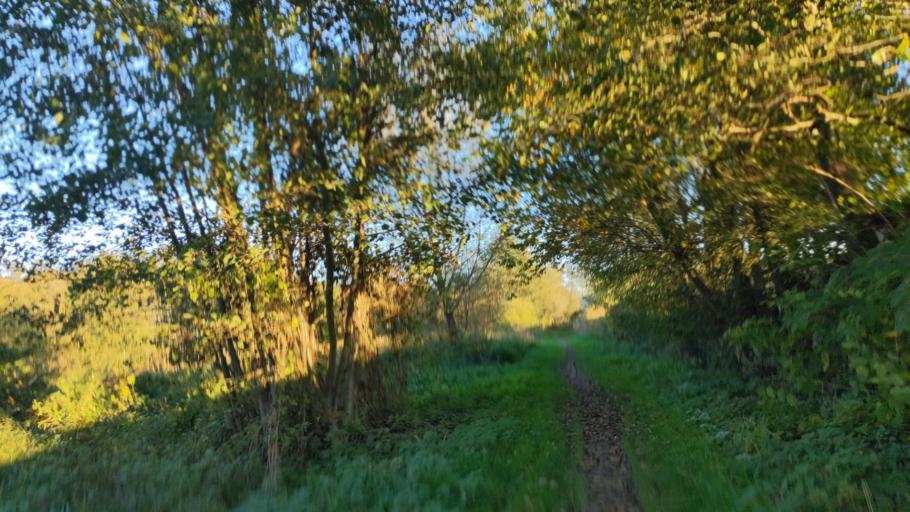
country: DE
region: Schleswig-Holstein
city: Gross Gronau
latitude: 53.7806
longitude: 10.7578
